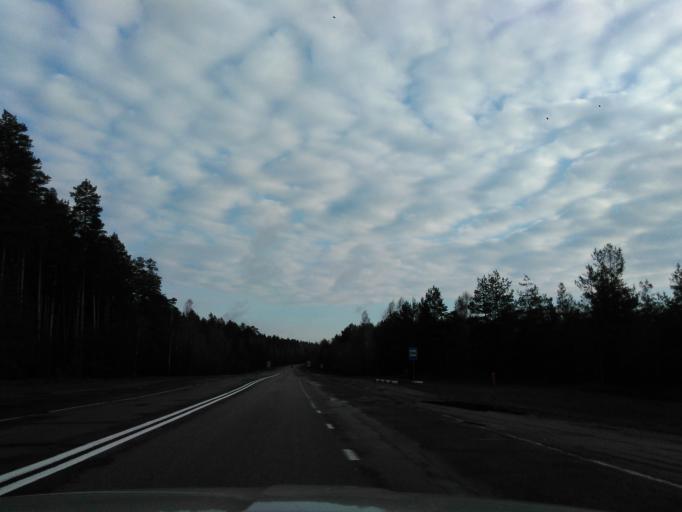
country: BY
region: Minsk
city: Plyeshchanitsy
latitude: 54.3489
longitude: 27.8794
